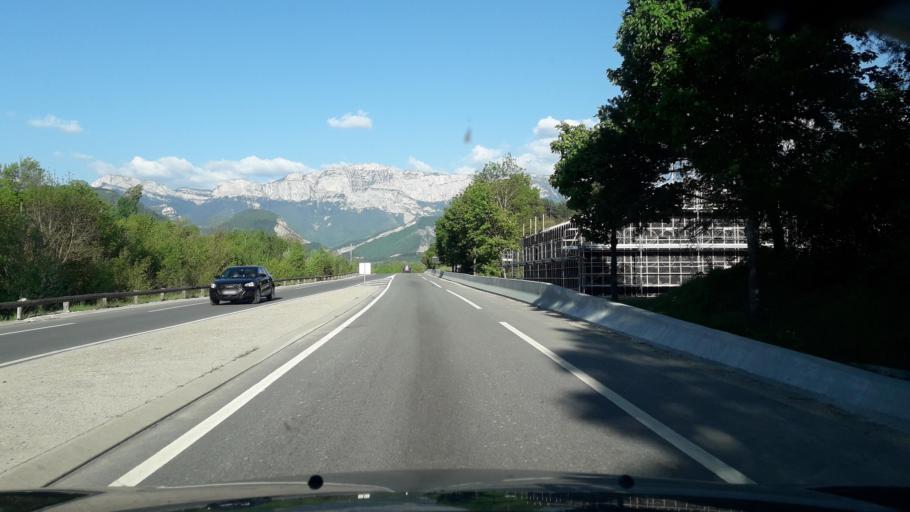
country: FR
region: Rhone-Alpes
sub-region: Departement de la Drome
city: Die
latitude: 44.7665
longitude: 5.3257
